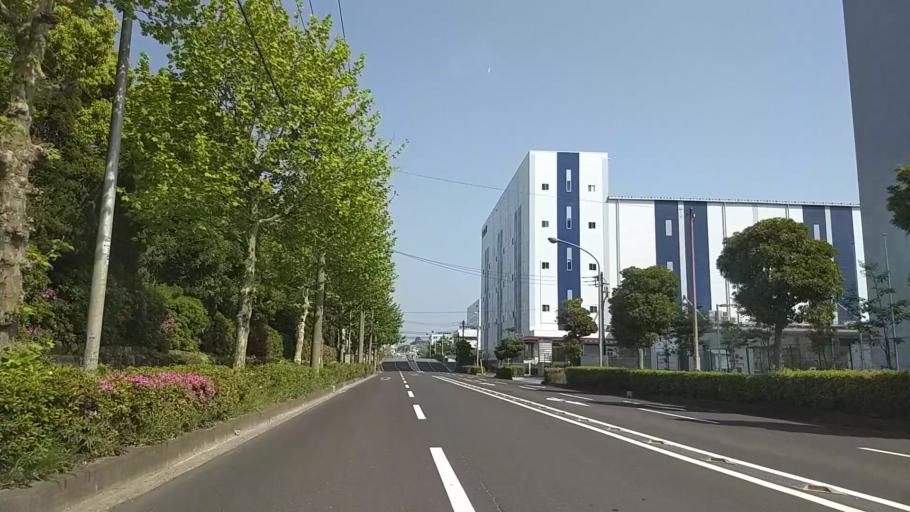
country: JP
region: Kanagawa
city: Yokohama
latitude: 35.4806
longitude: 139.6578
